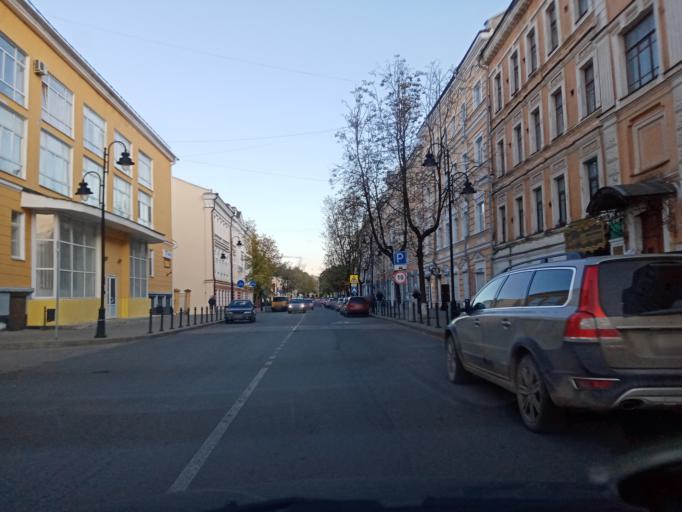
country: RU
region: Pskov
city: Pskov
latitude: 57.8181
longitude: 28.3356
